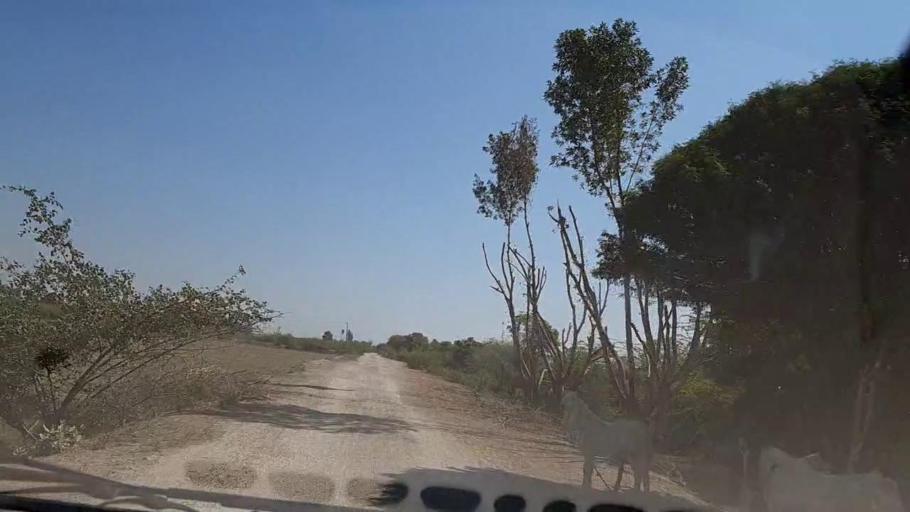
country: PK
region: Sindh
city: Mirpur Khas
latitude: 25.4242
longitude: 69.0383
